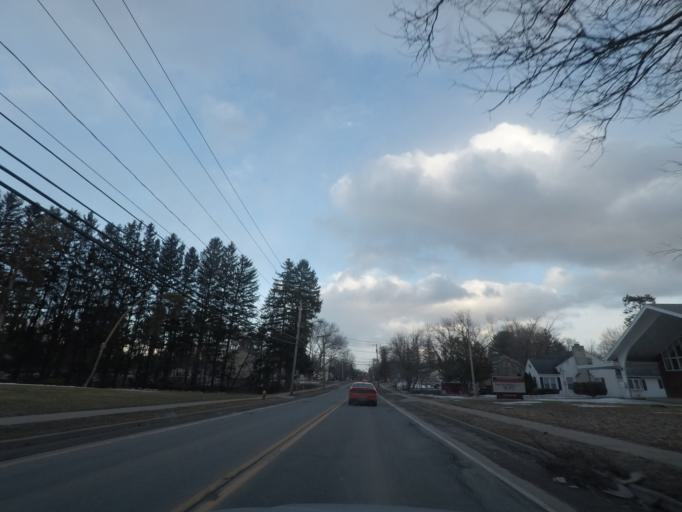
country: US
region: New York
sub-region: Oneida County
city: Utica
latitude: 43.1108
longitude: -75.1845
